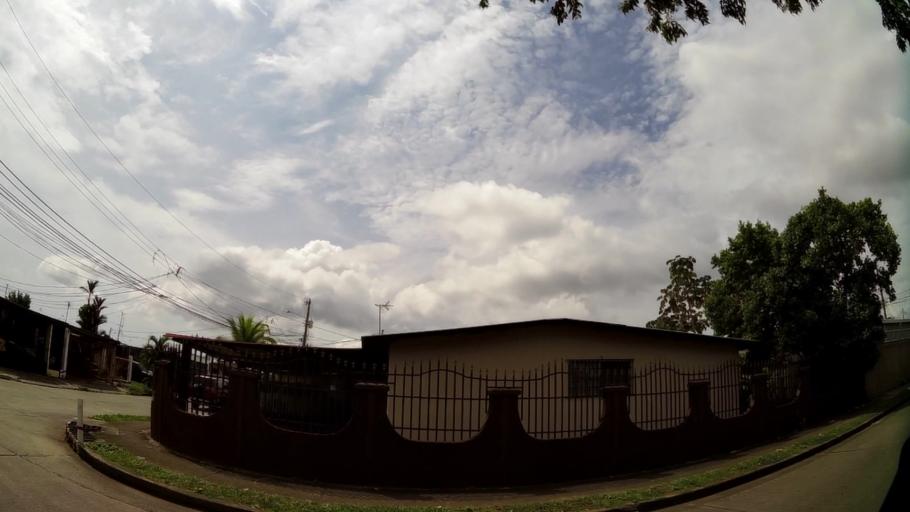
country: PA
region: Panama
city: San Miguelito
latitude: 9.0474
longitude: -79.4169
